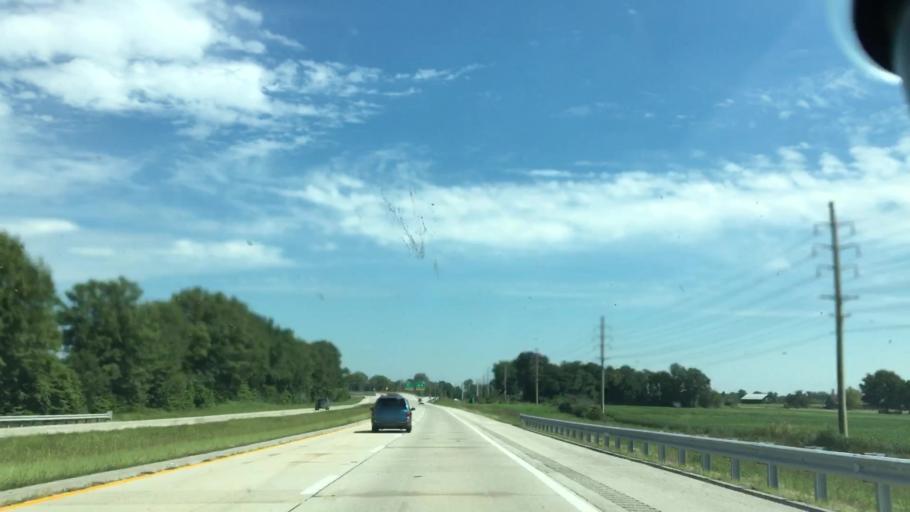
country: US
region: Kentucky
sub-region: Daviess County
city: Owensboro
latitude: 37.7656
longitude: -87.1735
